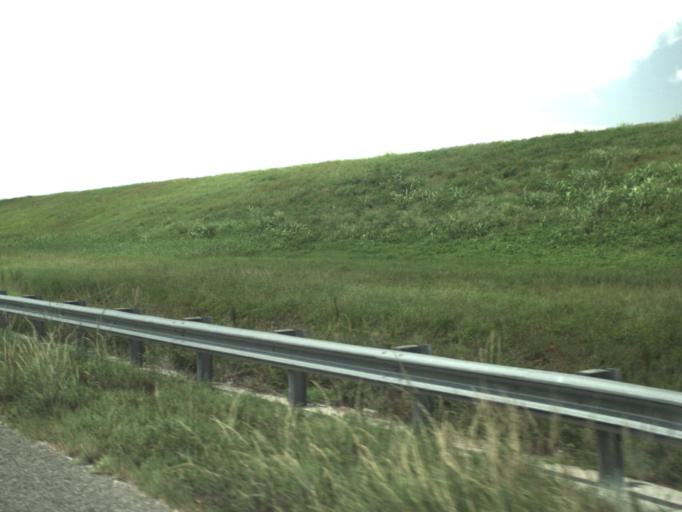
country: US
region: Florida
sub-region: Hendry County
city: Clewiston
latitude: 26.7313
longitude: -80.8600
